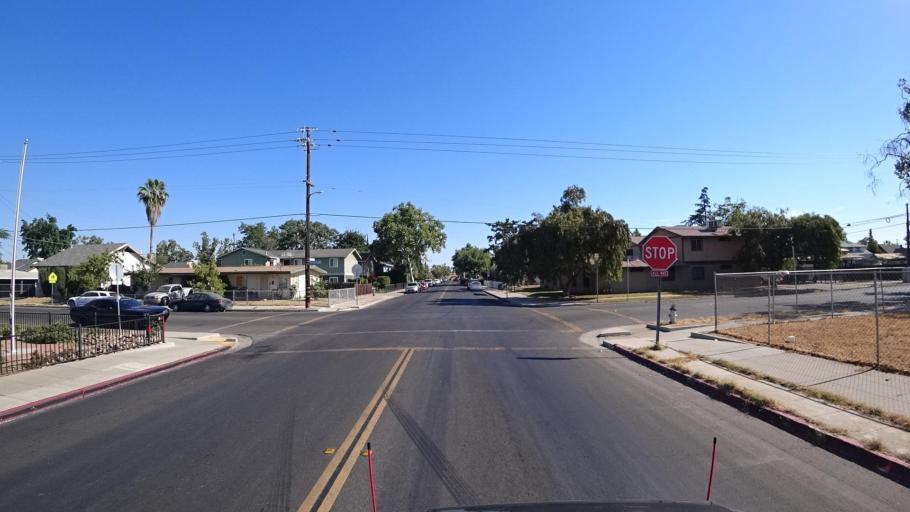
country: US
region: California
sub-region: Fresno County
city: Fresno
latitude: 36.7467
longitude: -119.7947
